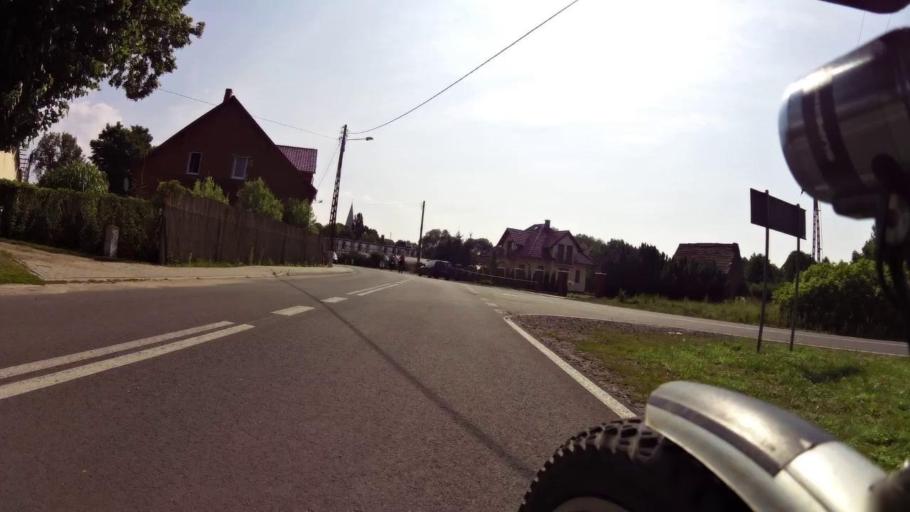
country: PL
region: West Pomeranian Voivodeship
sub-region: Powiat mysliborski
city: Boleszkowice
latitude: 52.6725
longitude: 14.5383
